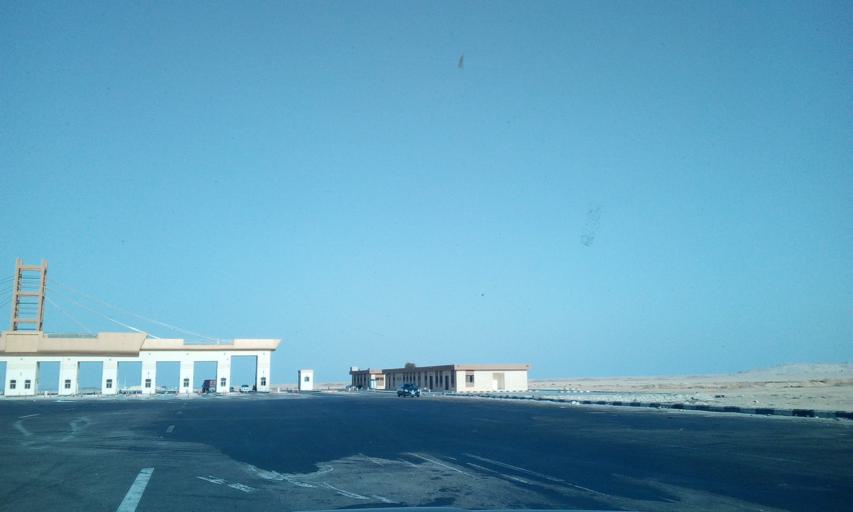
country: EG
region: As Suways
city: Ain Sukhna
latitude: 29.1103
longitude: 32.5483
